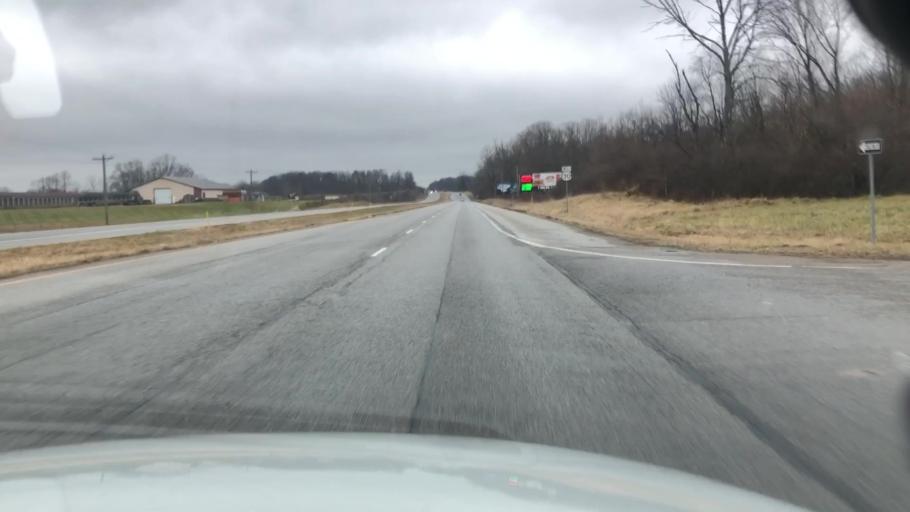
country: US
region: Indiana
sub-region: Whitley County
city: Columbia City
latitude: 41.1769
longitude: -85.5683
